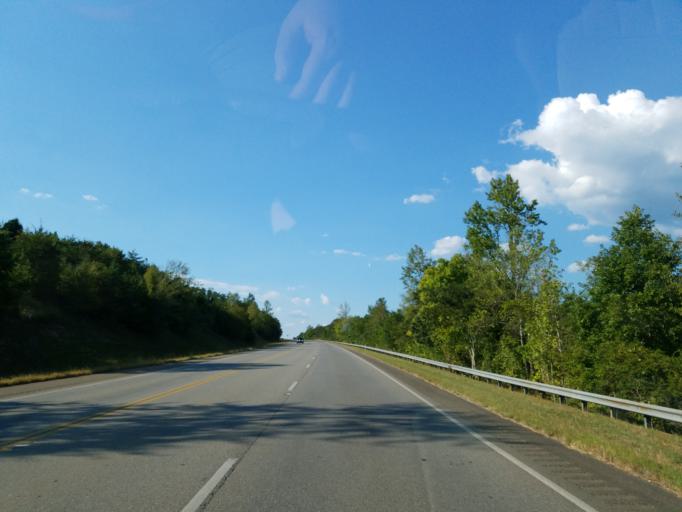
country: US
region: Georgia
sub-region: Murray County
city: Chatsworth
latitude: 34.6688
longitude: -84.7223
